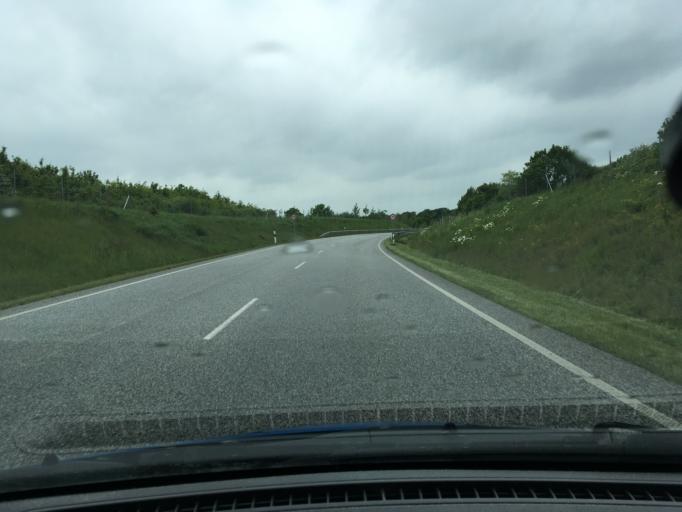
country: DE
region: Schleswig-Holstein
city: Gross Sarau
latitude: 53.7624
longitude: 10.7218
